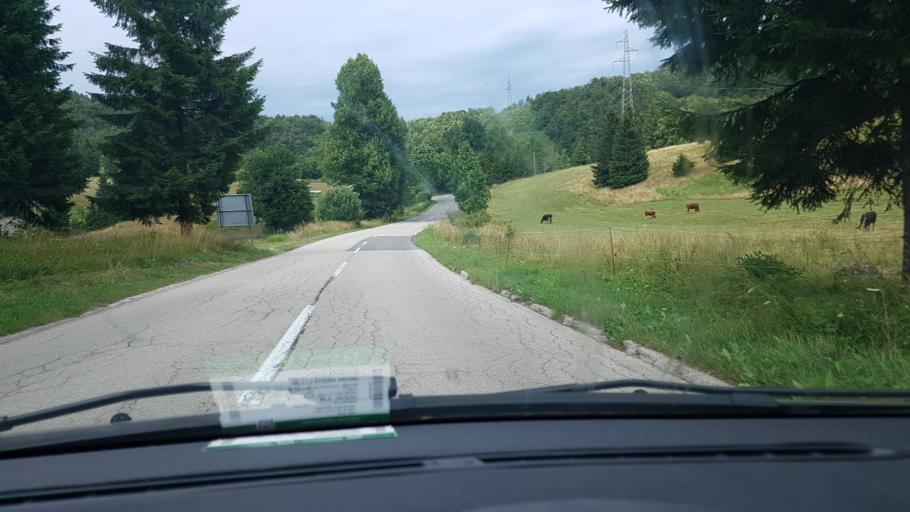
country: HR
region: Primorsko-Goranska
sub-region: Grad Delnice
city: Delnice
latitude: 45.3362
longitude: 14.7490
